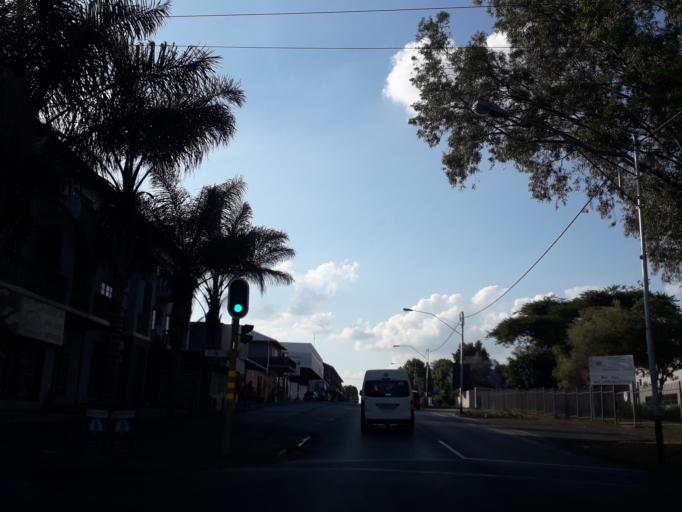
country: ZA
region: Gauteng
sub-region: City of Johannesburg Metropolitan Municipality
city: Johannesburg
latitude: -26.1374
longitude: 27.9951
